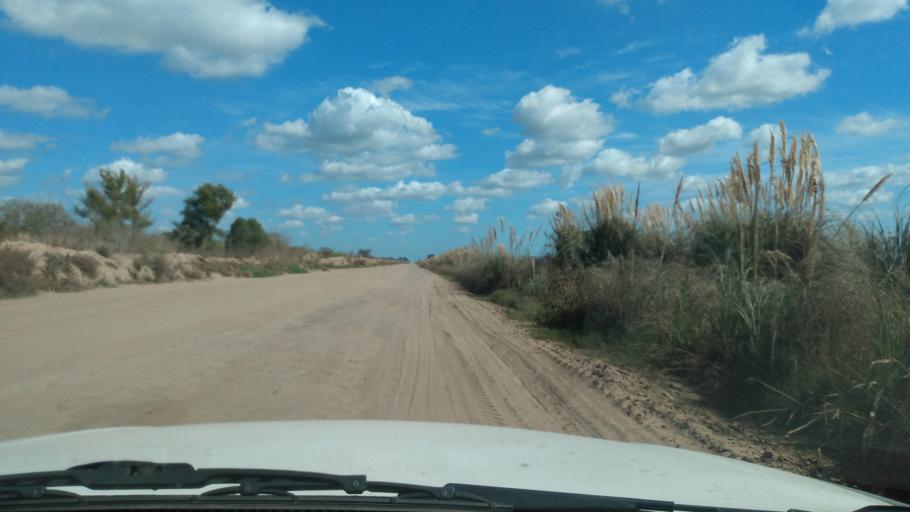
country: AR
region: Buenos Aires
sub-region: Partido de Navarro
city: Navarro
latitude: -35.0023
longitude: -59.3572
